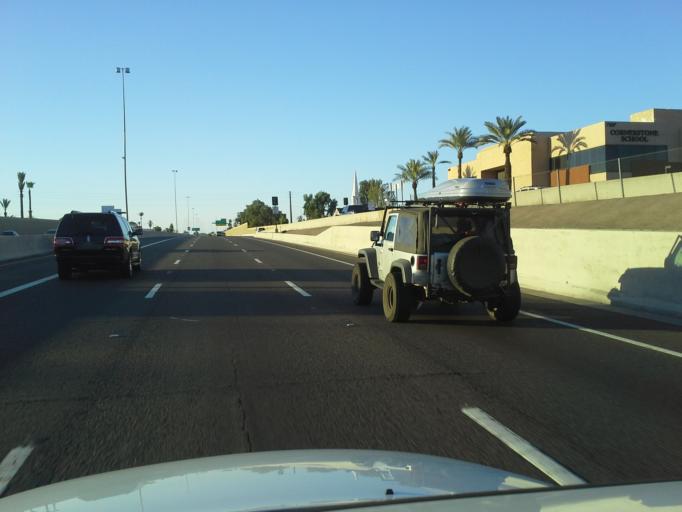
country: US
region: Arizona
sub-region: Maricopa County
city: Glendale
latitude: 33.5404
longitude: -112.1122
